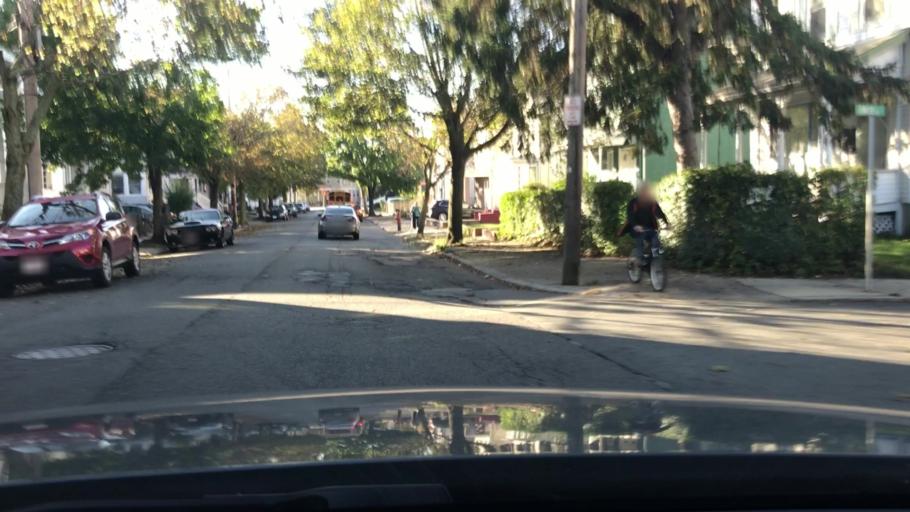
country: US
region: Massachusetts
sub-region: Middlesex County
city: Malden
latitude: 42.4308
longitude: -71.0623
